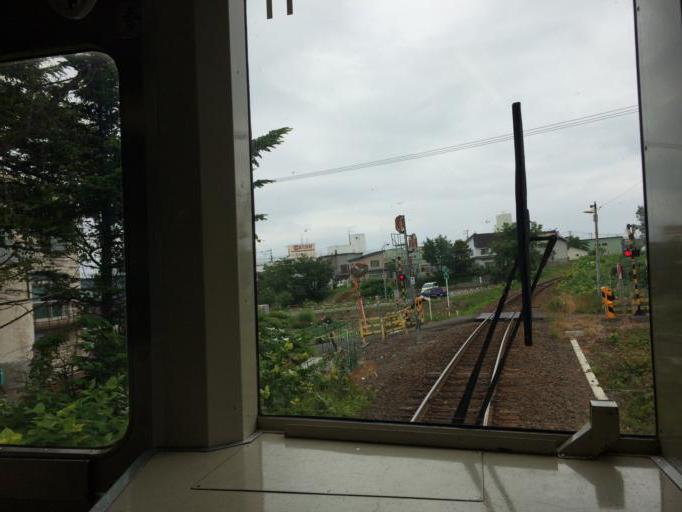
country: JP
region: Hokkaido
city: Yoichi
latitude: 43.1902
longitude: 140.7959
